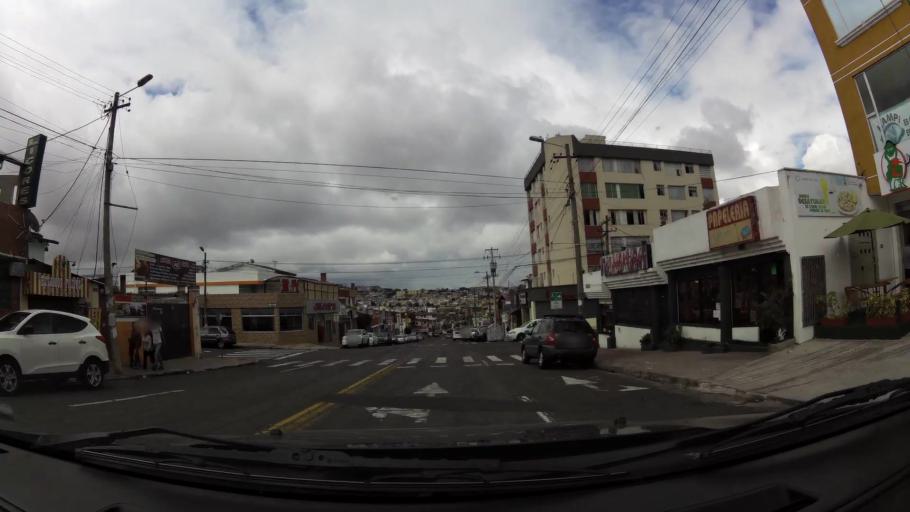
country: EC
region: Pichincha
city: Quito
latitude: -0.1292
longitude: -78.4997
